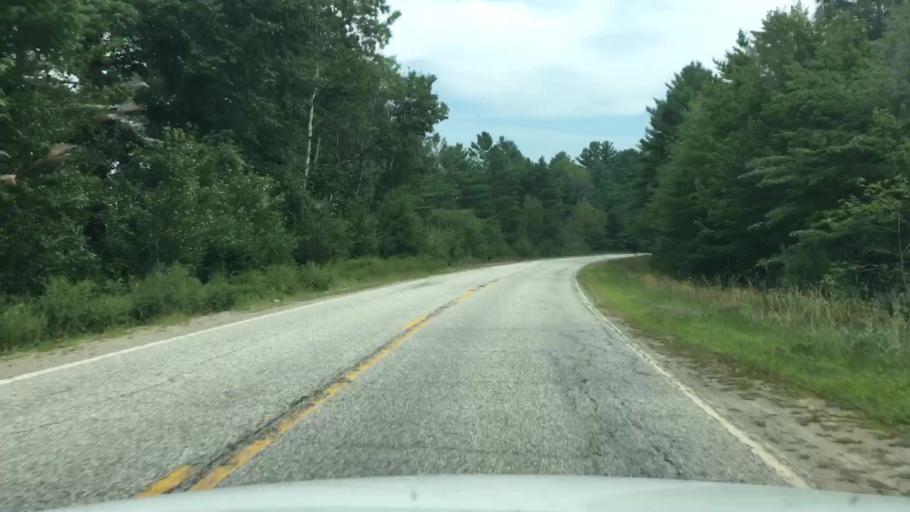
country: US
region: Maine
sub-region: Oxford County
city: Rumford
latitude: 44.6139
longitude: -70.7389
